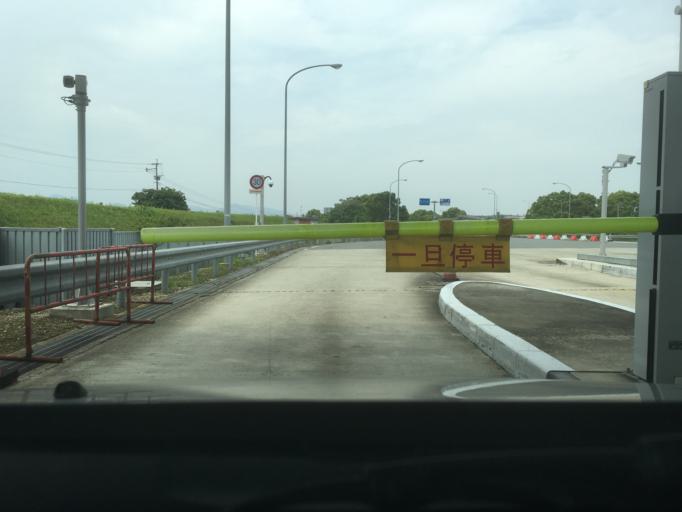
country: JP
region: Kumamoto
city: Kumamoto
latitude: 32.7914
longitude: 130.7876
